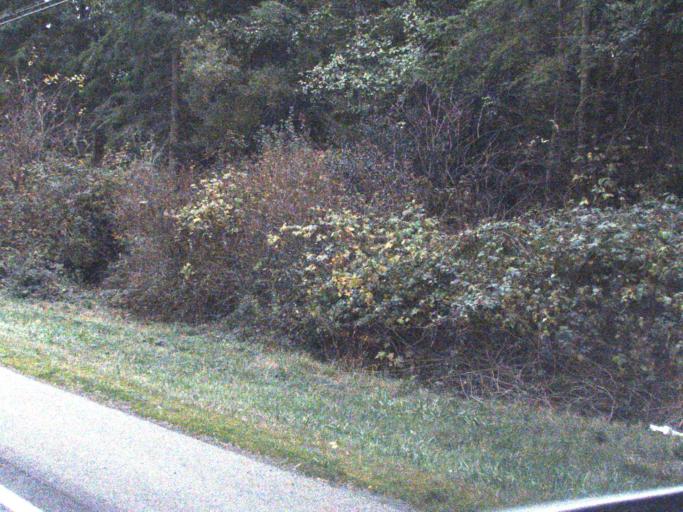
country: US
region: Washington
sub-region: Island County
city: Camano
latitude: 48.1609
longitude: -122.6045
